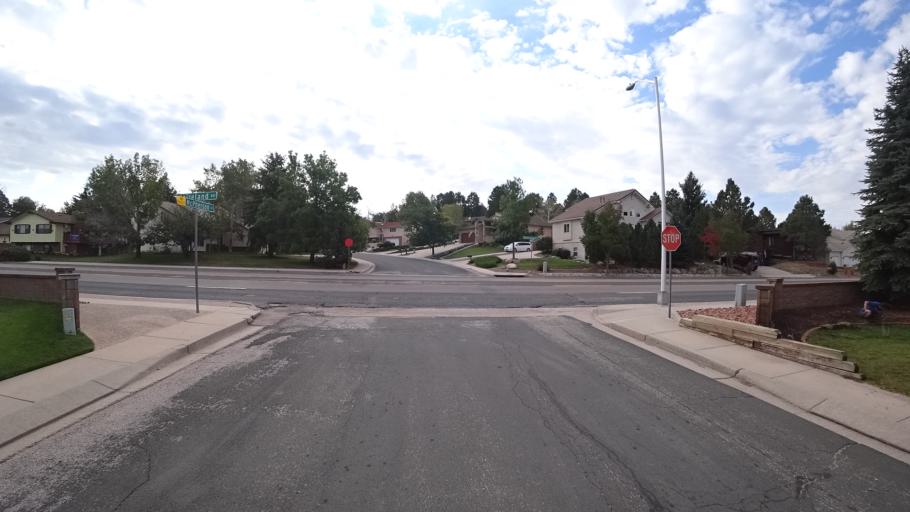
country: US
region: Colorado
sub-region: El Paso County
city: Cimarron Hills
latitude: 38.8706
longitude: -104.7513
